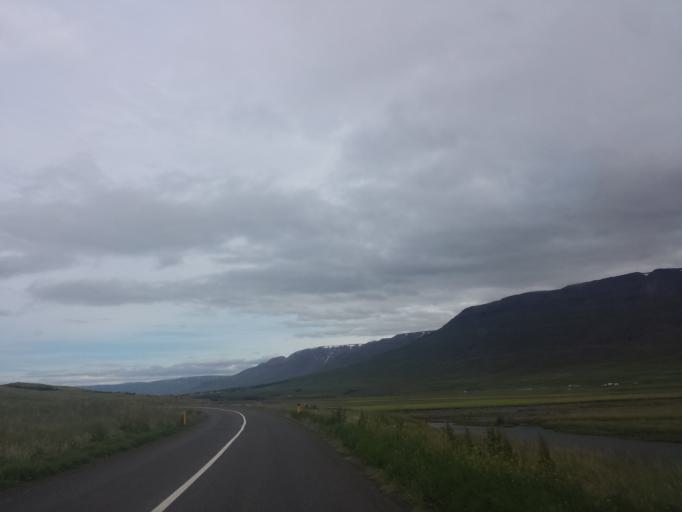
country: IS
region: Northeast
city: Akureyri
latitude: 65.4486
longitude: -18.2055
